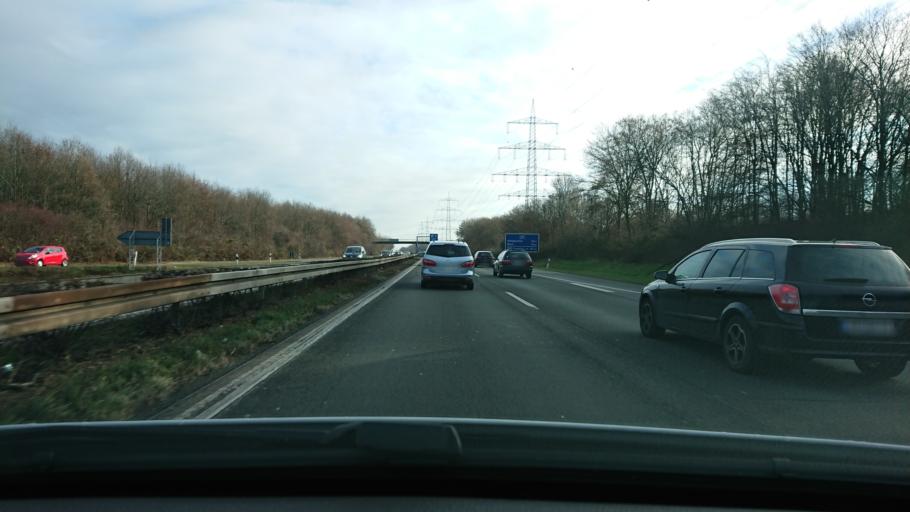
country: DE
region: North Rhine-Westphalia
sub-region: Regierungsbezirk Koln
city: Troisdorf
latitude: 50.8176
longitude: 7.1123
